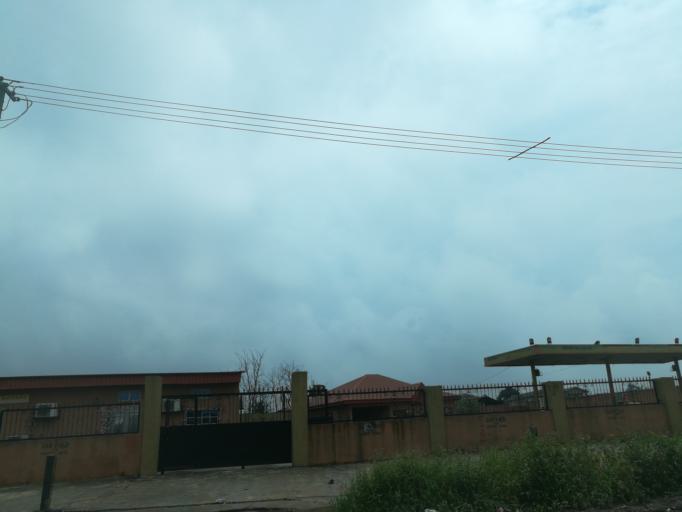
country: NG
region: Lagos
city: Ikorodu
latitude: 6.6638
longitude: 3.5188
